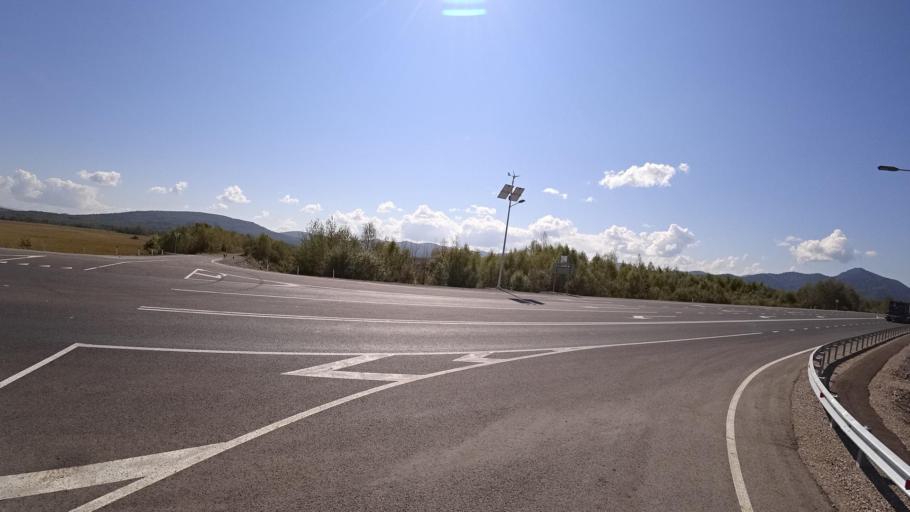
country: RU
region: Jewish Autonomous Oblast
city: Londoko
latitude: 49.0026
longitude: 131.9455
